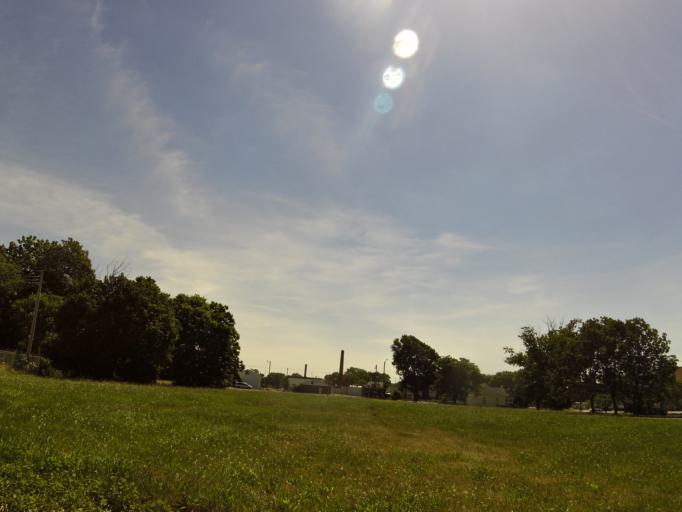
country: US
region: Illinois
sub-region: Vermilion County
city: Danville
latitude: 40.1352
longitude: -87.6328
